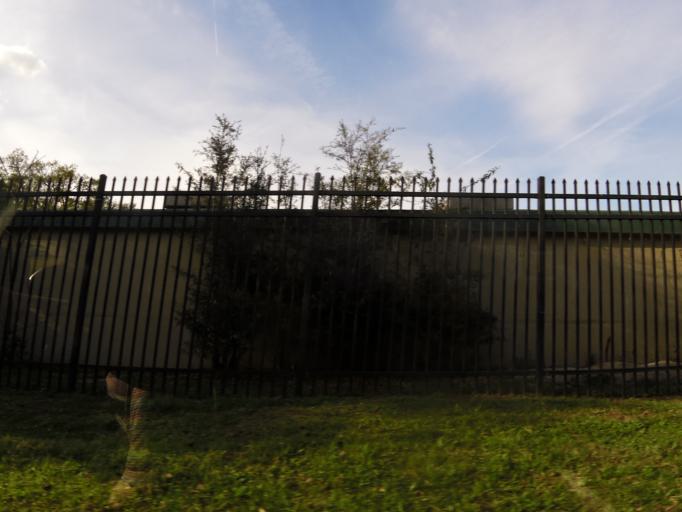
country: US
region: Florida
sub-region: Duval County
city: Jacksonville
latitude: 30.3560
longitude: -81.6872
